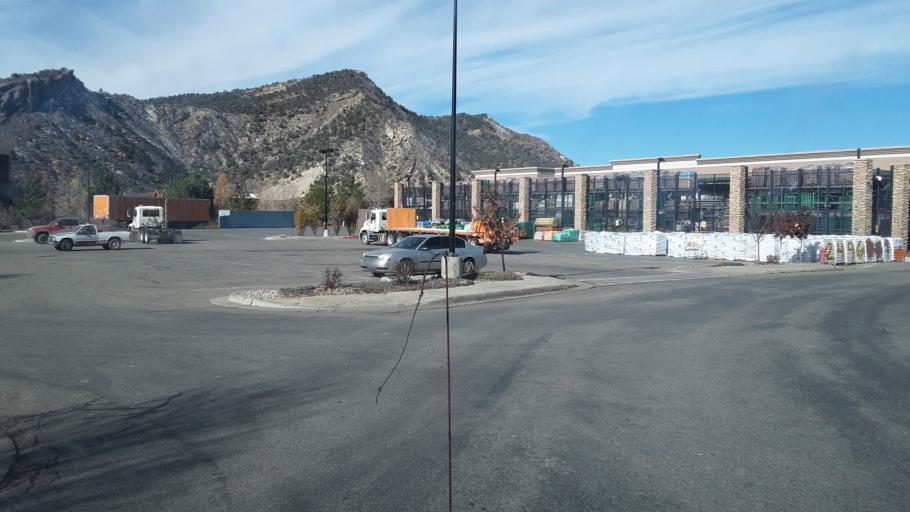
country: US
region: Colorado
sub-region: La Plata County
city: Durango
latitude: 37.2233
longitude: -107.8586
